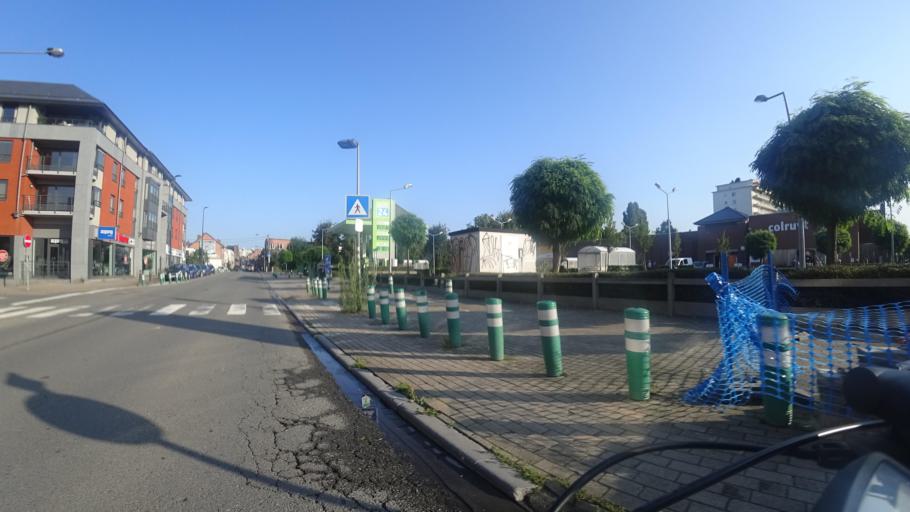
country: BE
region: Wallonia
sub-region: Province du Brabant Wallon
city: Wavre
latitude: 50.7168
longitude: 4.6159
